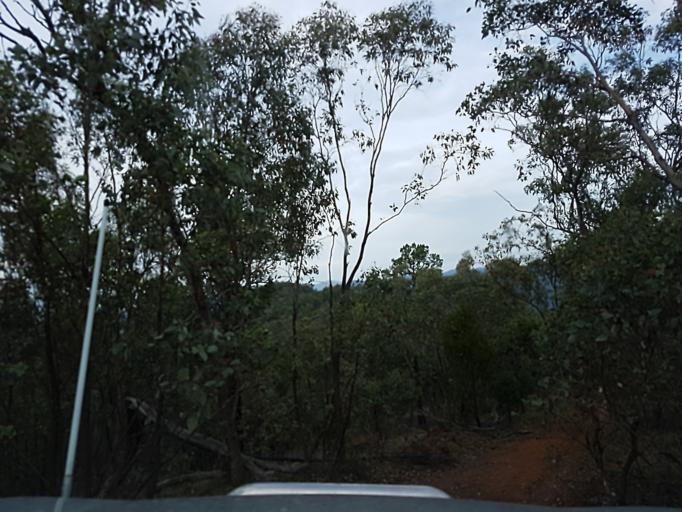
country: AU
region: New South Wales
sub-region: Snowy River
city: Jindabyne
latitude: -36.9566
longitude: 148.3800
